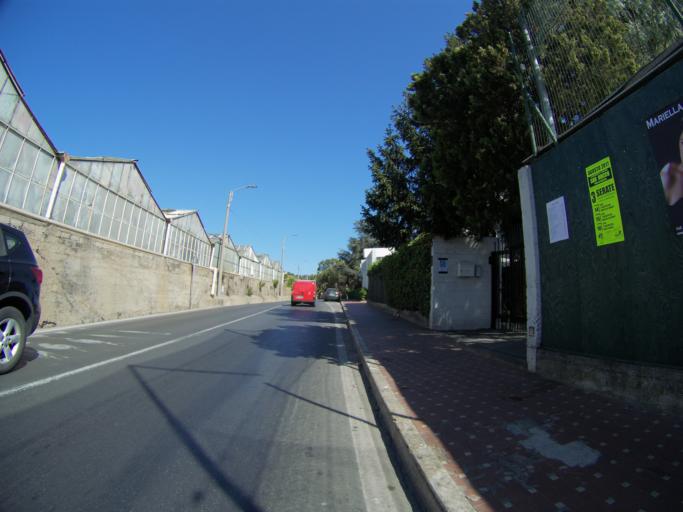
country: IT
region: Liguria
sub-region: Provincia di Imperia
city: Vallecrosia
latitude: 43.7899
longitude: 7.6387
